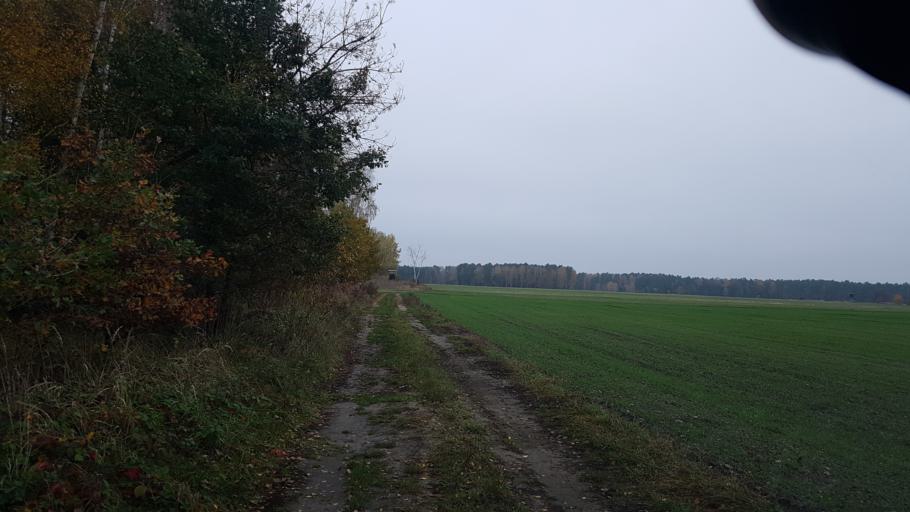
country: DE
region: Brandenburg
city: Ruckersdorf
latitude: 51.5692
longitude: 13.6460
